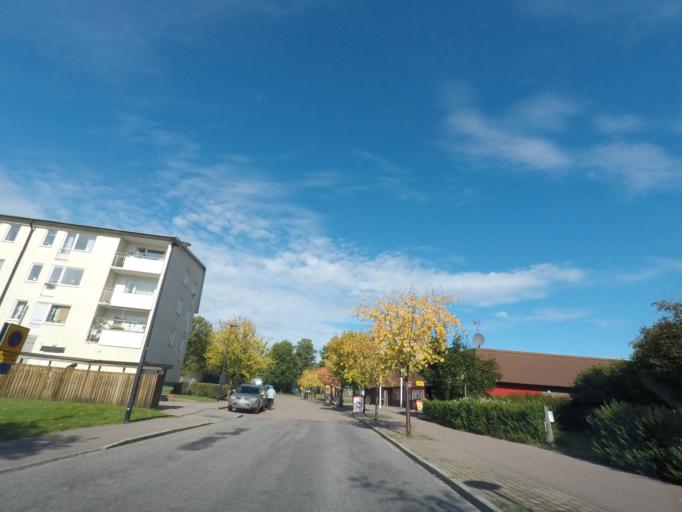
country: SE
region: Vaestmanland
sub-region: Skinnskattebergs Kommun
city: Skinnskatteberg
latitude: 59.8315
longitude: 15.6932
